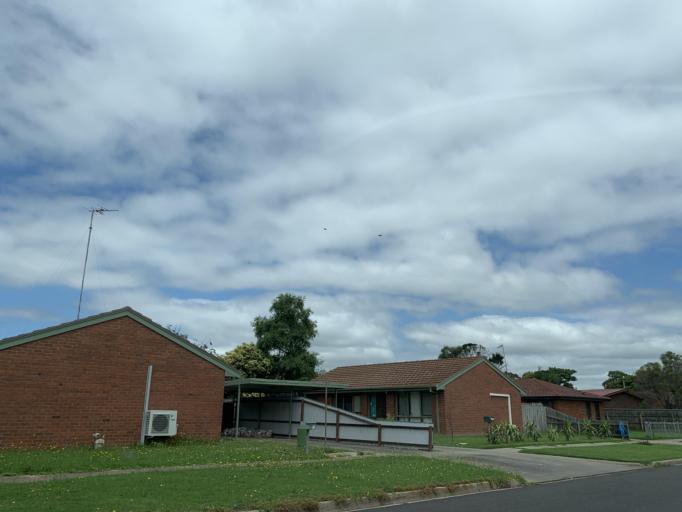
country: AU
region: Victoria
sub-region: Wellington
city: Sale
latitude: -38.1051
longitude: 147.0898
